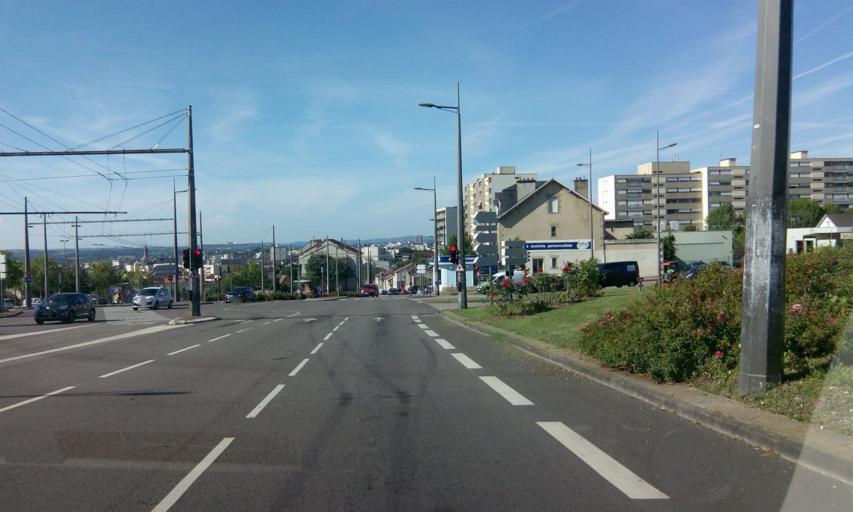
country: FR
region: Limousin
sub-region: Departement de la Haute-Vienne
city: Limoges
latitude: 45.8524
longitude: 1.2651
